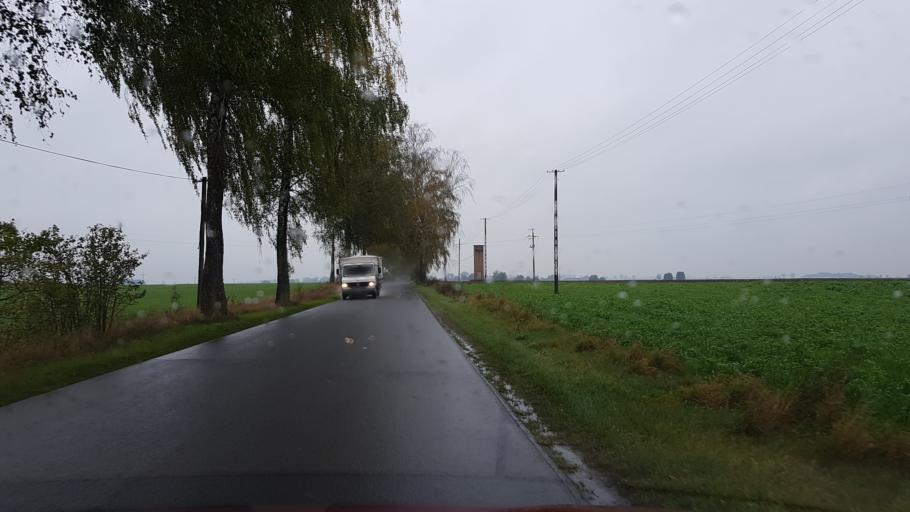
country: PL
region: Greater Poland Voivodeship
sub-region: Powiat zlotowski
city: Krajenka
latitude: 53.3107
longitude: 16.9705
